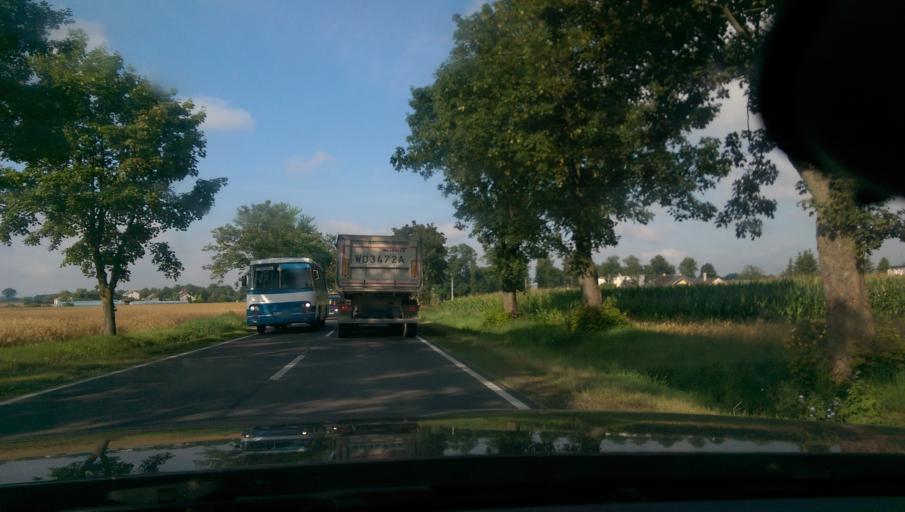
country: PL
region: Masovian Voivodeship
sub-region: Powiat ciechanowski
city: Opinogora Gorna
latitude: 52.9214
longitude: 20.6634
